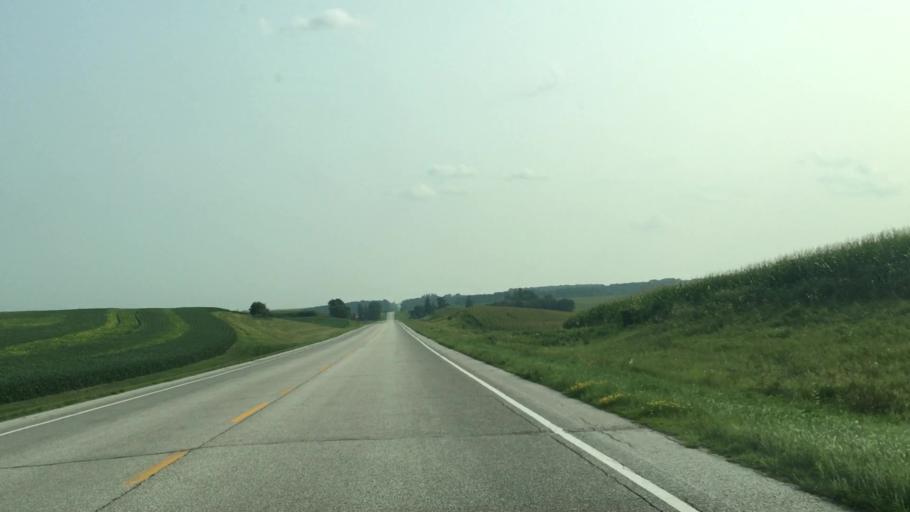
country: US
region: Minnesota
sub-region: Fillmore County
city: Harmony
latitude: 43.6137
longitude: -91.9298
